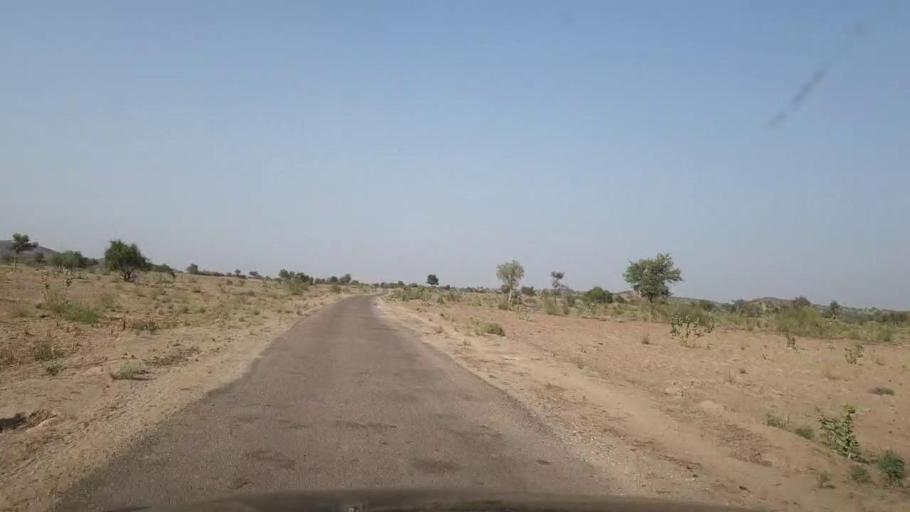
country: PK
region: Sindh
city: Islamkot
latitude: 25.1281
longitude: 70.5159
